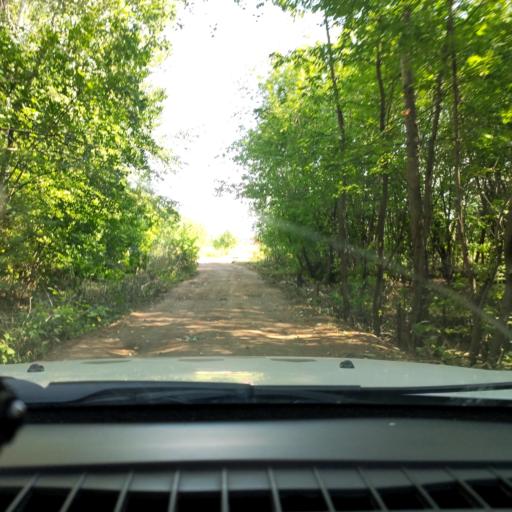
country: RU
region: Samara
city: Smyshlyayevka
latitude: 53.2048
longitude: 50.3300
